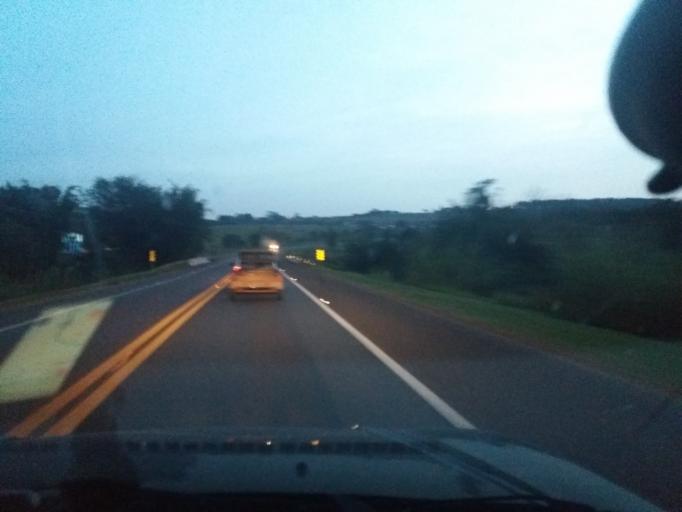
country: BR
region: Sao Paulo
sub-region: Itapeva
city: Itapeva
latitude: -23.9771
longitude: -48.8451
